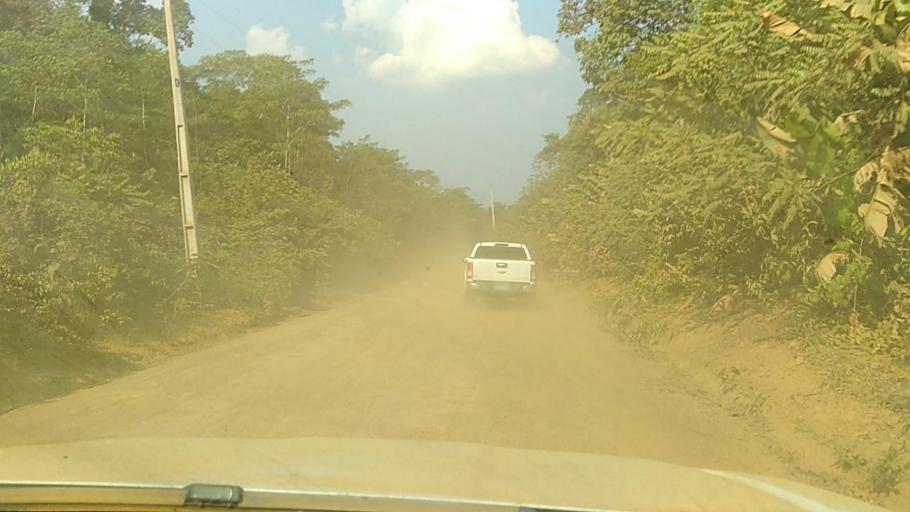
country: BR
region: Rondonia
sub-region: Porto Velho
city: Porto Velho
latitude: -8.6704
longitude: -64.0115
